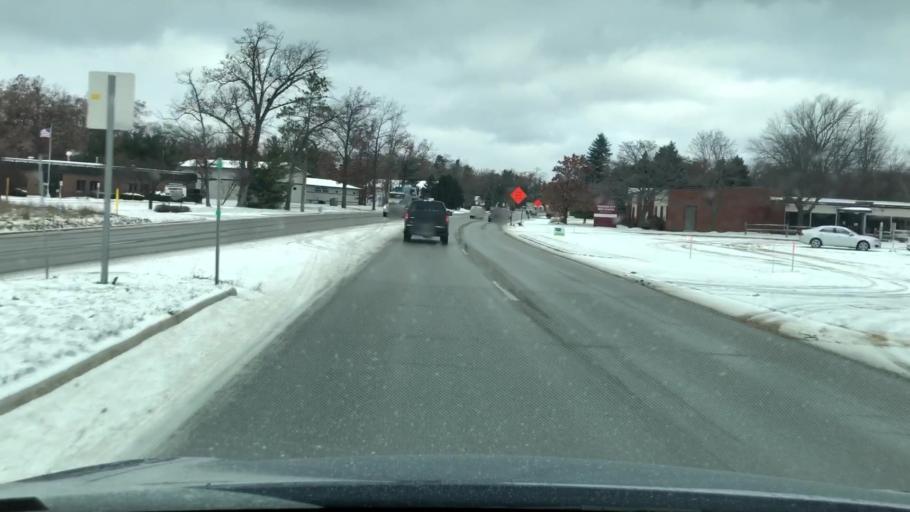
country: US
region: Michigan
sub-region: Grand Traverse County
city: Traverse City
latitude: 44.7416
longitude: -85.5600
